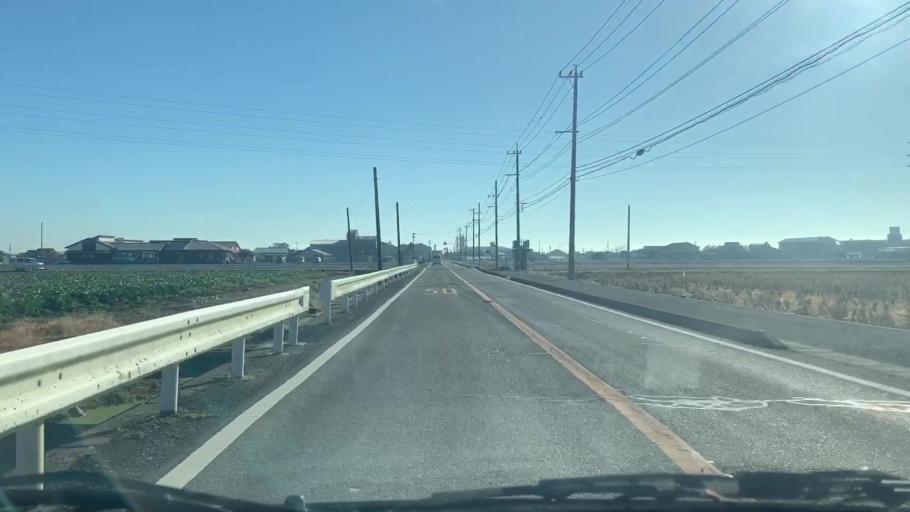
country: JP
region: Saga Prefecture
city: Kashima
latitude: 33.1916
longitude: 130.1270
